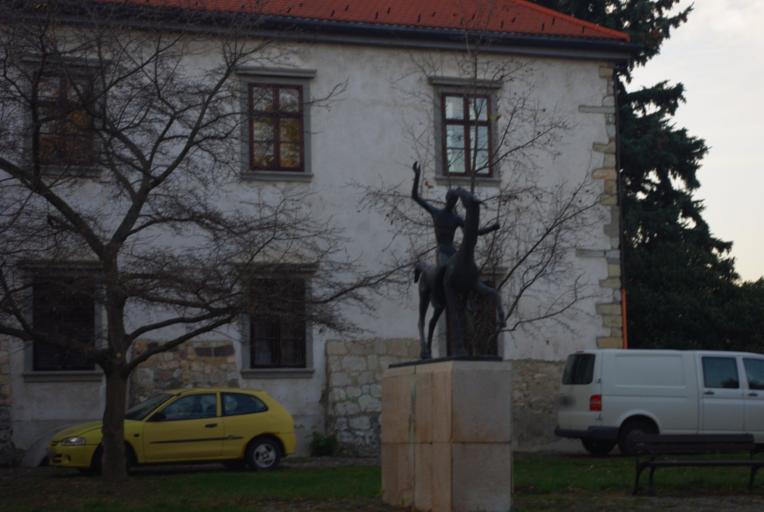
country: HU
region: Borsod-Abauj-Zemplen
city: Sarospatak
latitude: 48.3177
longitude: 21.5687
